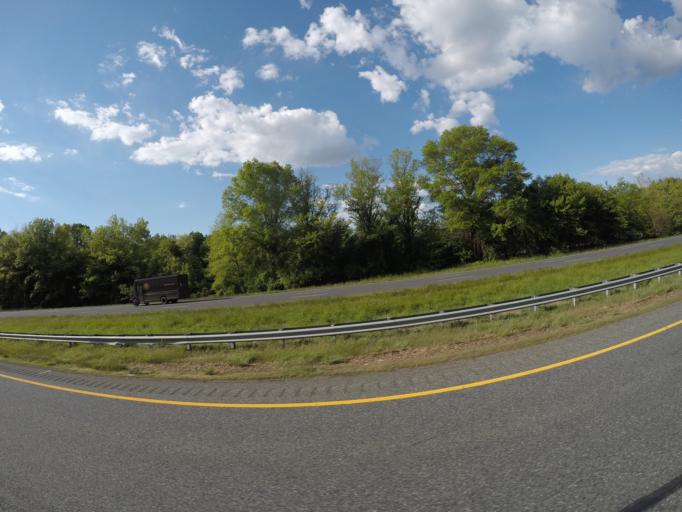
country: US
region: Maryland
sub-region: Carroll County
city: Mount Airy
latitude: 39.3475
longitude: -77.1005
